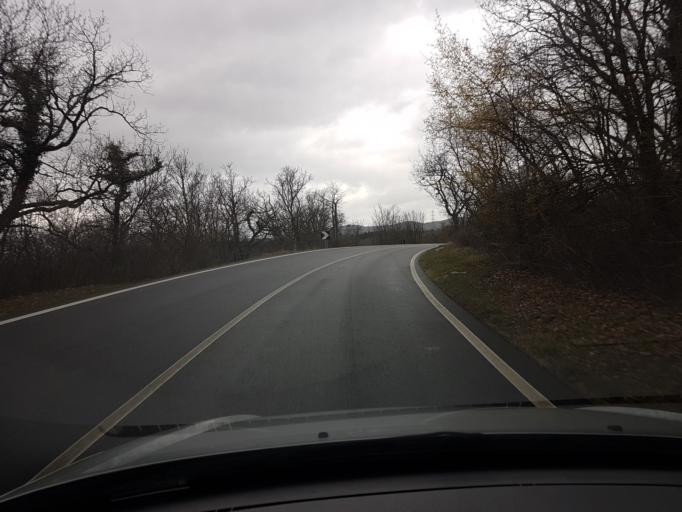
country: IT
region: Friuli Venezia Giulia
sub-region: Provincia di Trieste
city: Sgonico
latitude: 45.7389
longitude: 13.7225
